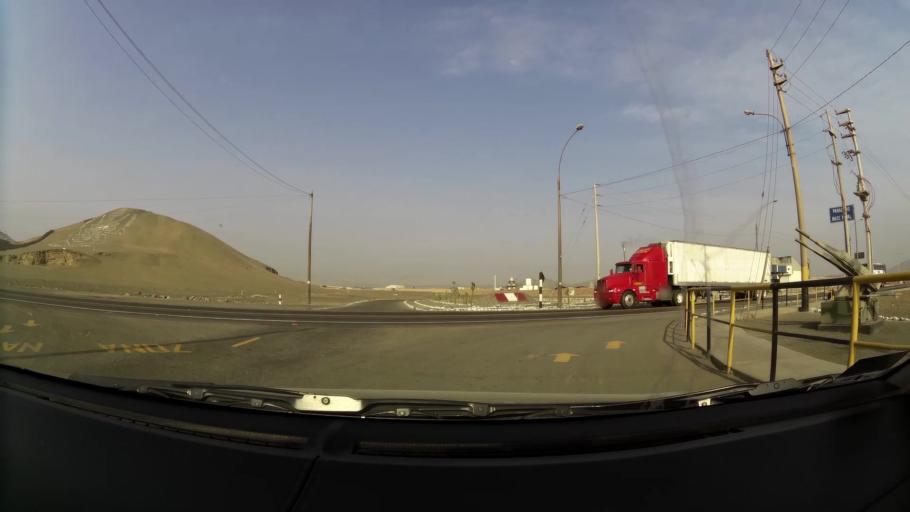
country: PE
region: Lima
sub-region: Lima
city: Santa Rosa
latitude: -11.7492
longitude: -77.1636
